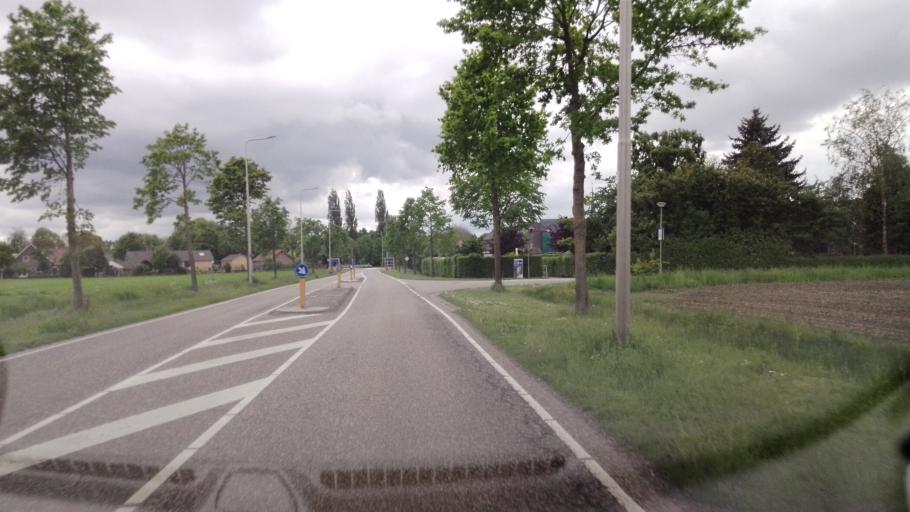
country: NL
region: Limburg
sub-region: Gemeente Venlo
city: Venlo
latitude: 51.4249
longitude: 6.1416
